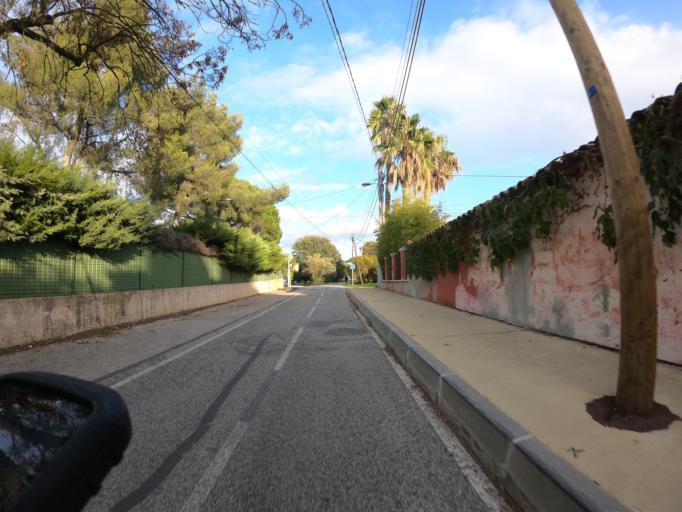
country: FR
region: Provence-Alpes-Cote d'Azur
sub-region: Departement du Var
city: La Garde
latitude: 43.1117
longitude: 5.9923
